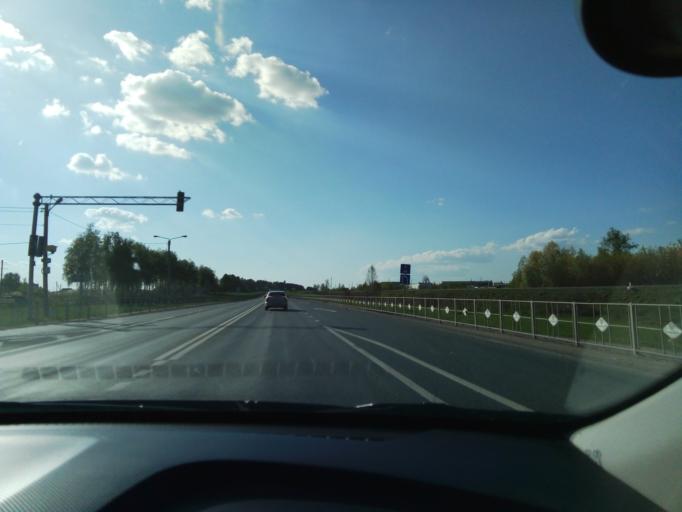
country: RU
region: Chuvashia
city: Novyye Lapsary
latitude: 56.0612
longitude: 47.2509
